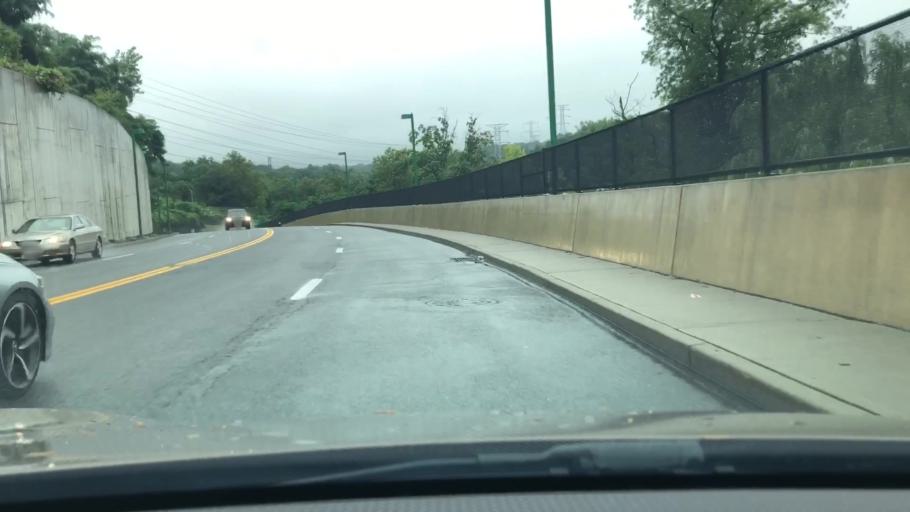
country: US
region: New York
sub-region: Westchester County
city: Tuckahoe
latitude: 40.9559
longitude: -73.8574
